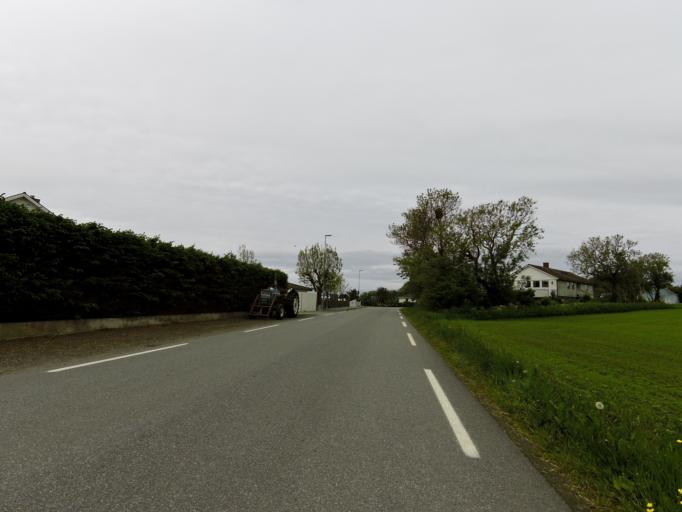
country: NO
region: Rogaland
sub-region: Klepp
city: Kleppe
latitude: 58.8176
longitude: 5.5688
